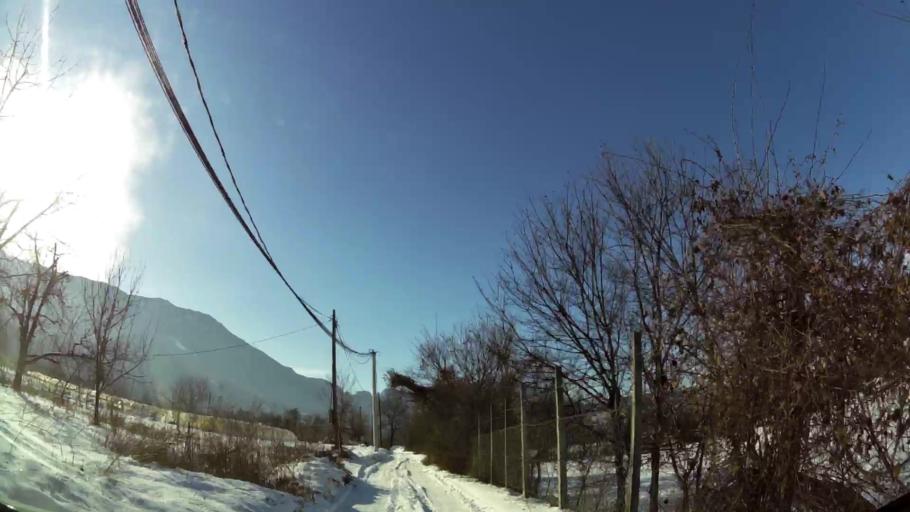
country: MK
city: Grchec
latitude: 41.9868
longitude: 21.3248
